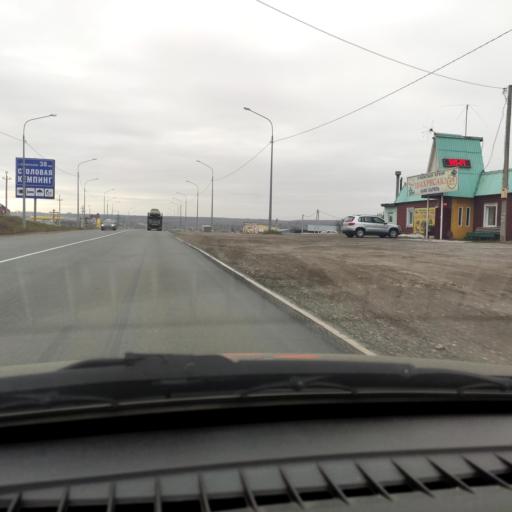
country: RU
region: Samara
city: Zhigulevsk
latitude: 53.3743
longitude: 49.4566
